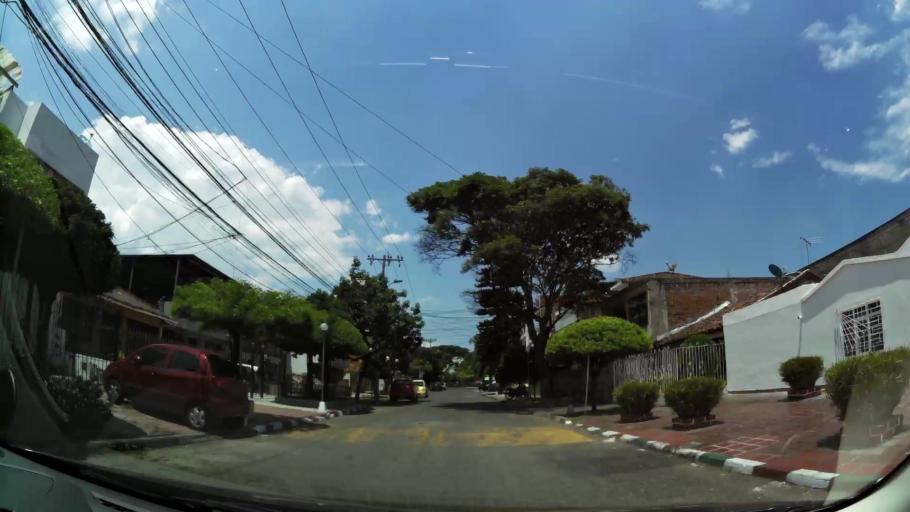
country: CO
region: Valle del Cauca
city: Cali
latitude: 3.4515
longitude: -76.4995
